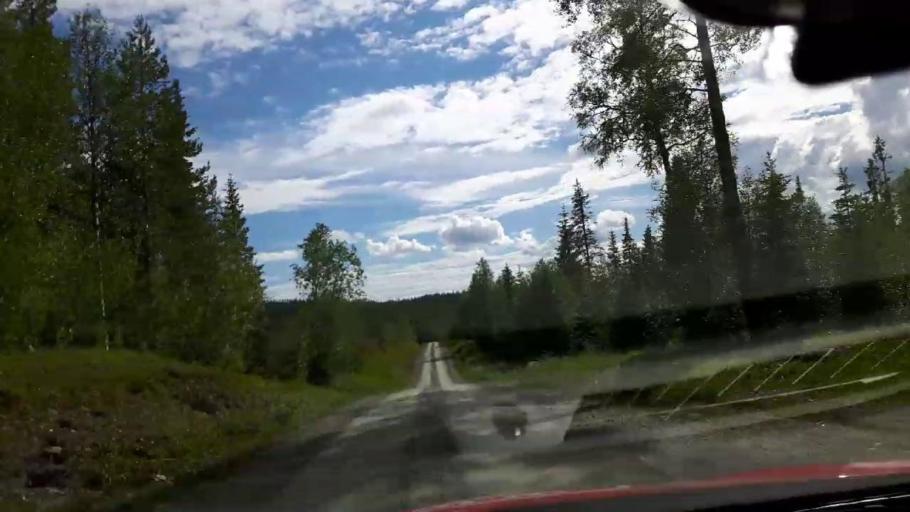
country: SE
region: Jaemtland
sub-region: Krokoms Kommun
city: Valla
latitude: 63.8965
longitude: 14.1755
